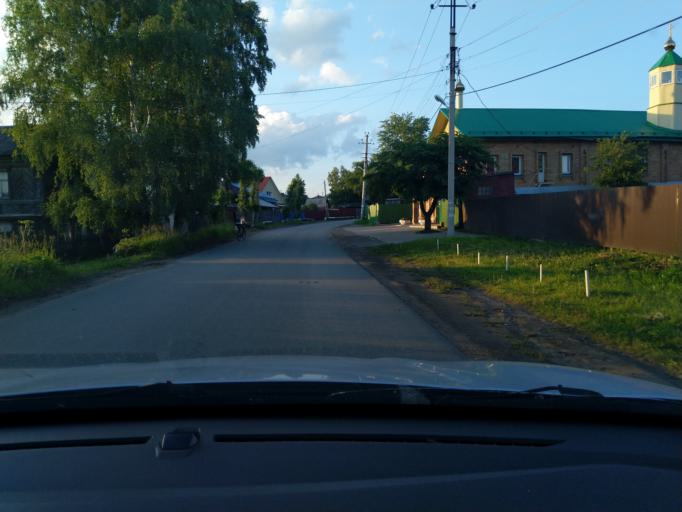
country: RU
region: Perm
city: Dobryanka
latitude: 58.4617
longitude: 56.4123
